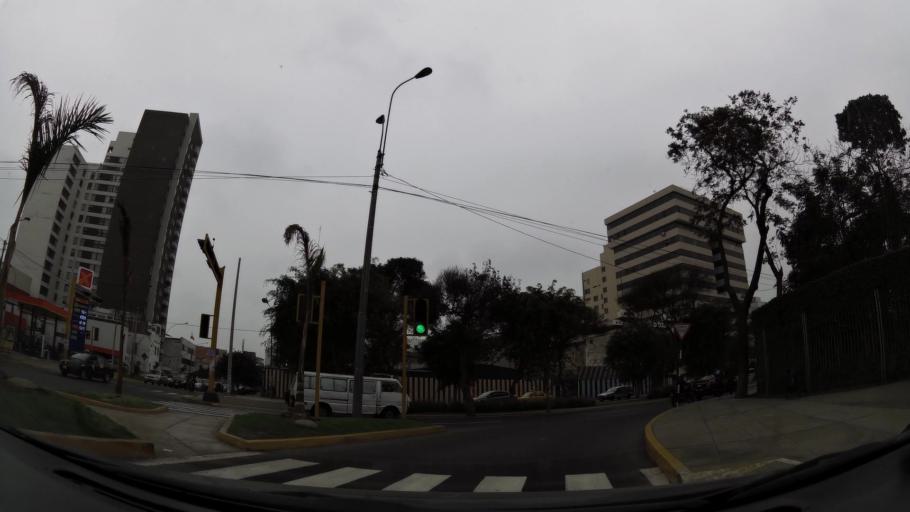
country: PE
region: Lima
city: Lima
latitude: -12.0733
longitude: -77.0359
